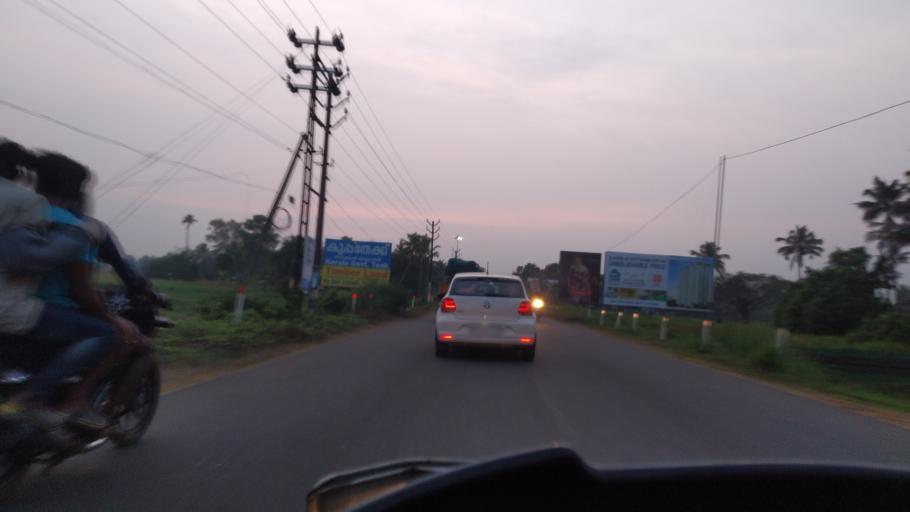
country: IN
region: Kerala
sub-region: Kottayam
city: Kottayam
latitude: 9.5921
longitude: 76.4507
